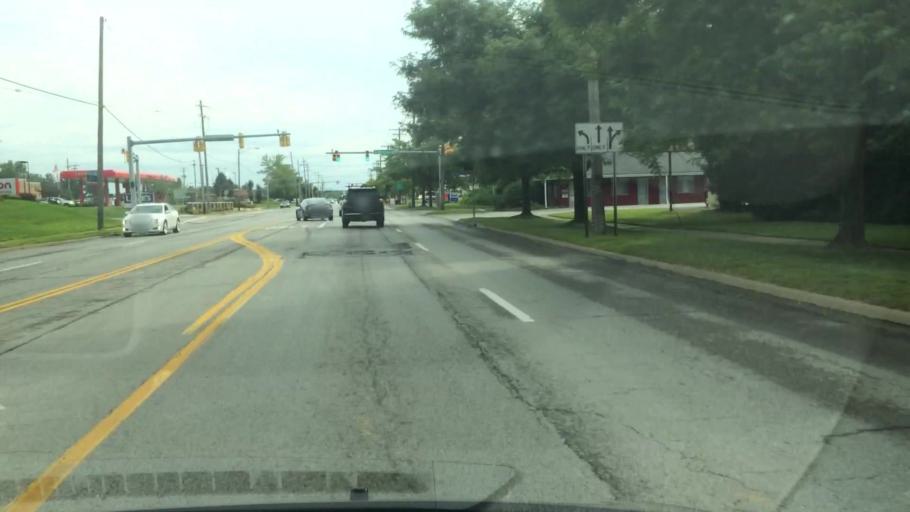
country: US
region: Ohio
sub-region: Cuyahoga County
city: Middleburg Heights
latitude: 41.3451
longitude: -81.8250
